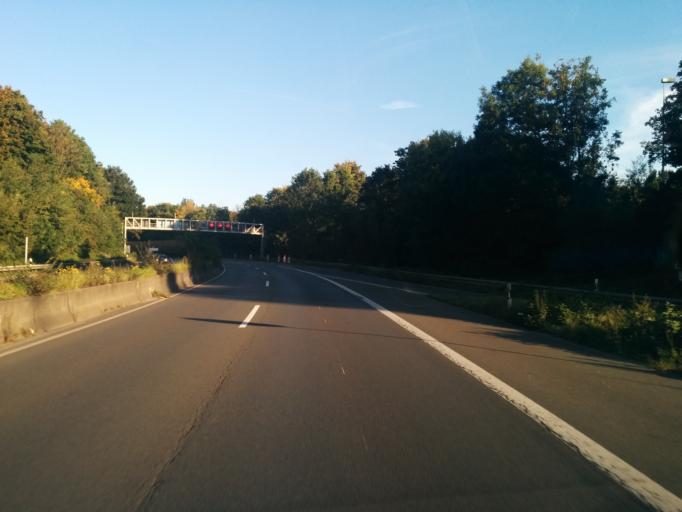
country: DE
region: North Rhine-Westphalia
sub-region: Regierungsbezirk Arnsberg
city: Bochum
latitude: 51.4947
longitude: 7.2333
